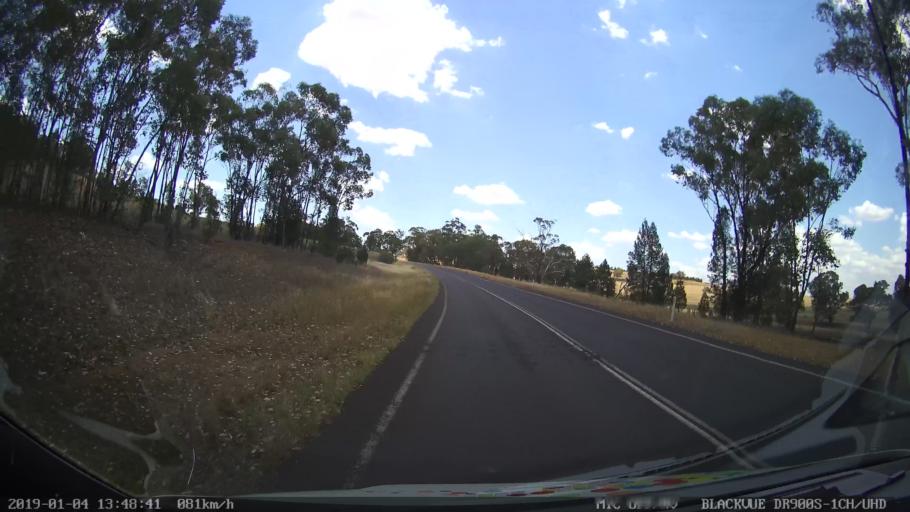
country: AU
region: New South Wales
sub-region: Dubbo Municipality
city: Dubbo
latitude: -32.4396
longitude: 148.5845
